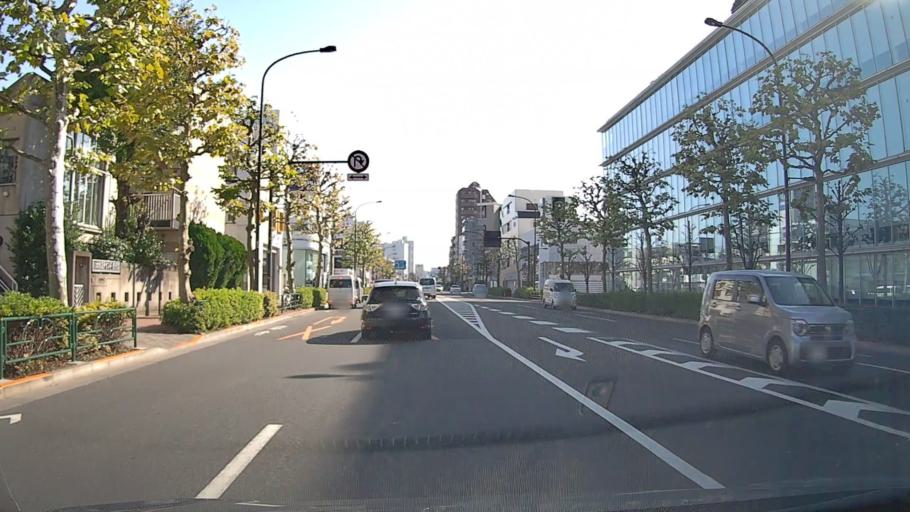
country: JP
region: Tokyo
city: Tokyo
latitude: 35.7308
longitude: 139.6749
